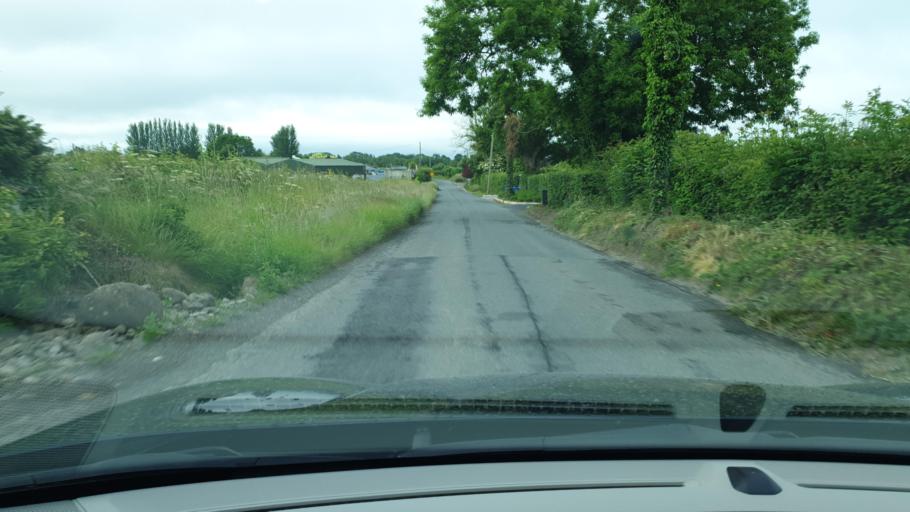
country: IE
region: Leinster
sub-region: An Mhi
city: Ashbourne
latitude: 53.5442
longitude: -6.4110
